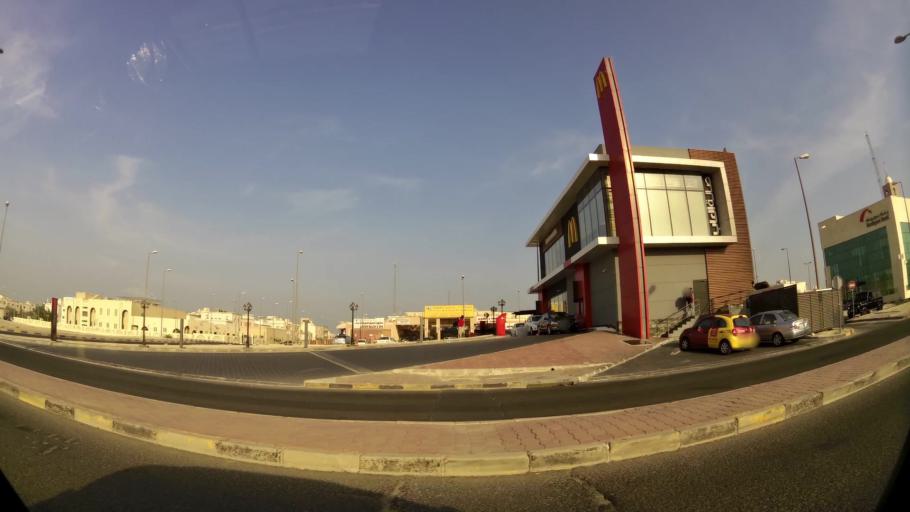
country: KW
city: Al Funaytis
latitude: 29.2357
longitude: 48.0780
